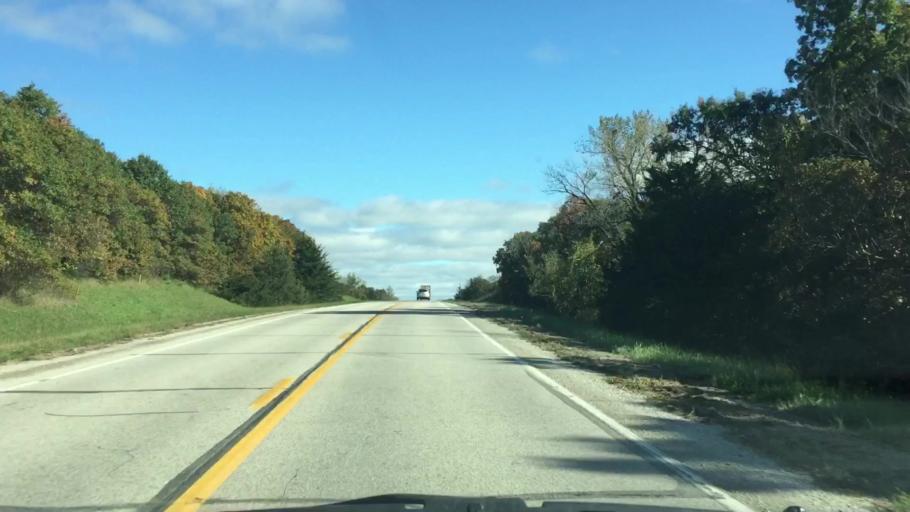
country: US
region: Iowa
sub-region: Decatur County
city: Leon
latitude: 40.6706
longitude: -93.7900
